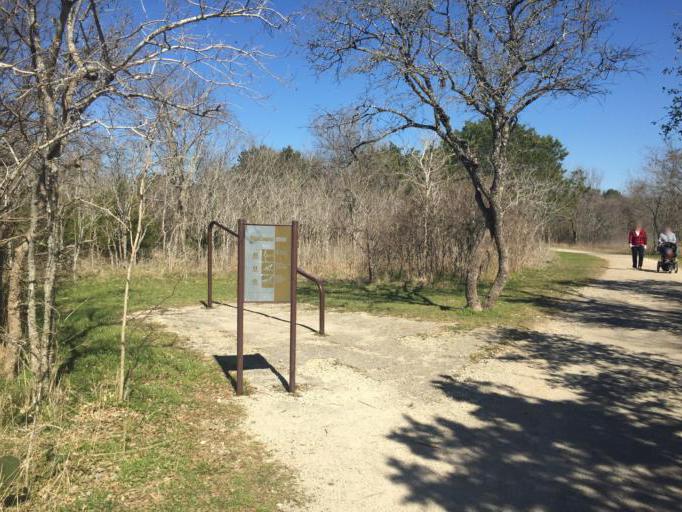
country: US
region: Texas
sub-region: Travis County
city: Onion Creek
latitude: 30.1564
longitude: -97.8063
